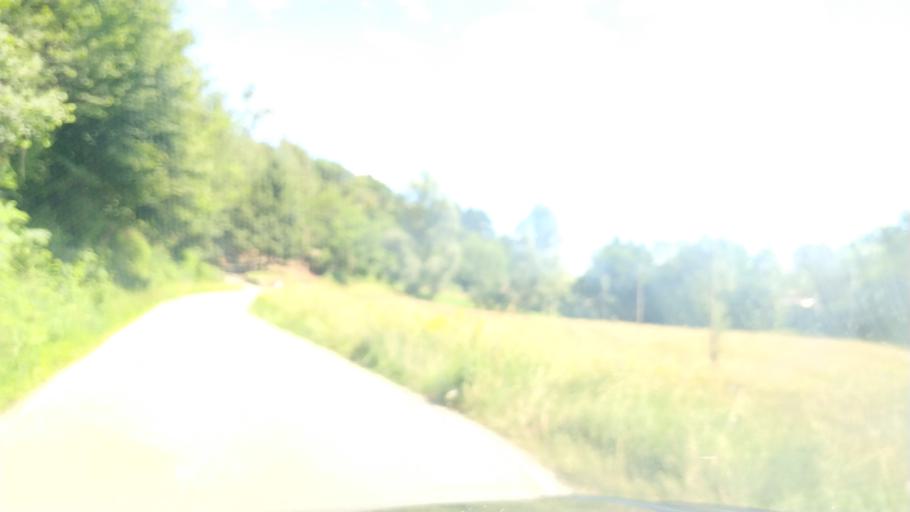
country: IT
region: Piedmont
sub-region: Provincia di Torino
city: Baldissero Canavese
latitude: 45.4081
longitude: 7.7219
